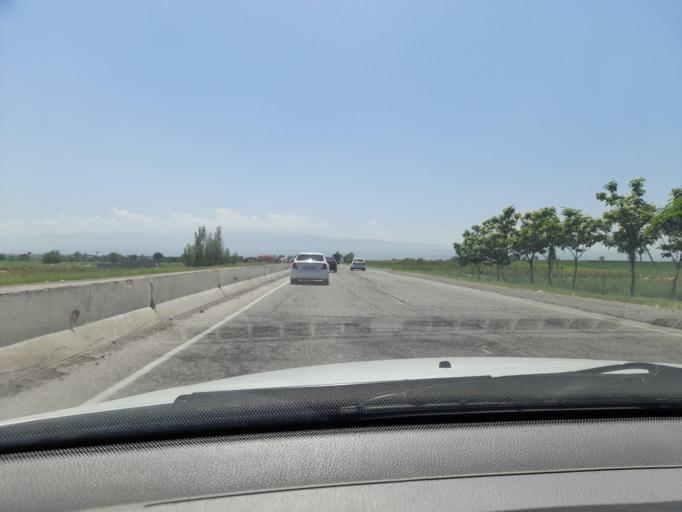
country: UZ
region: Jizzax
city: Jizzax
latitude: 40.1423
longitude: 67.9552
